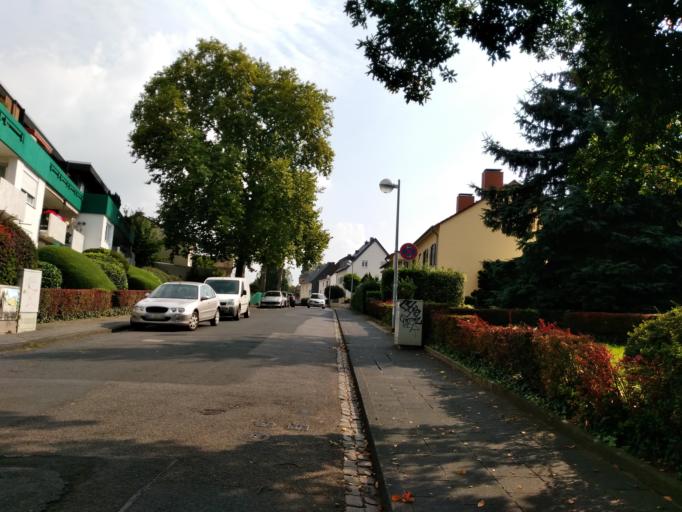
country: DE
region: North Rhine-Westphalia
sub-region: Regierungsbezirk Koln
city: Bad Honnef
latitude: 50.6422
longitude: 7.2241
